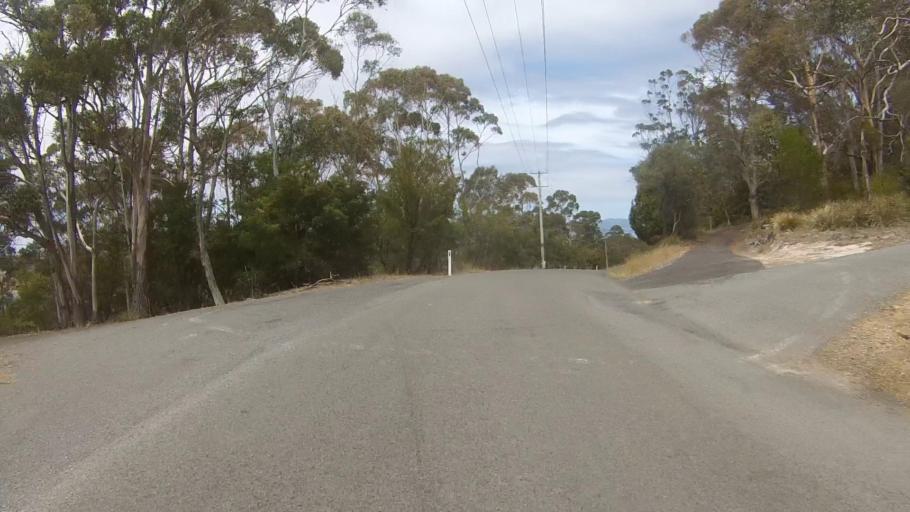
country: AU
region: Tasmania
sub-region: Kingborough
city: Blackmans Bay
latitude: -43.0507
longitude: 147.3405
